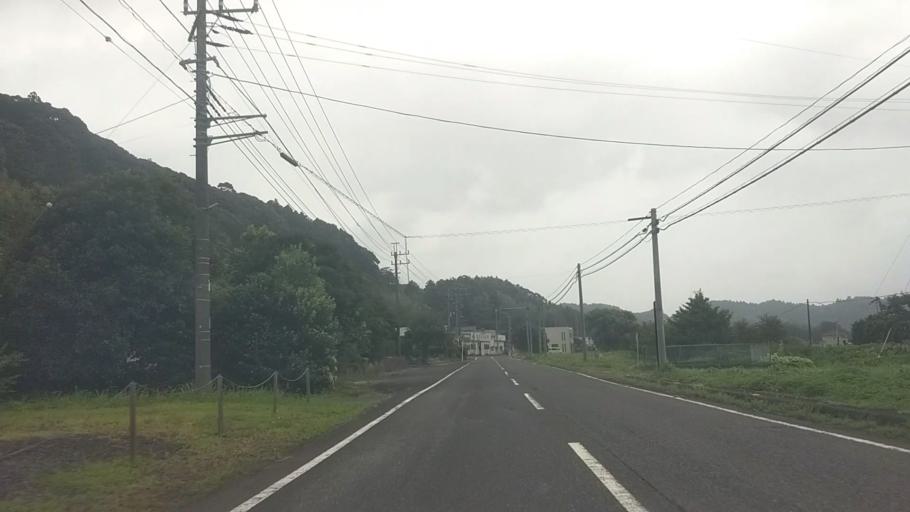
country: JP
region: Chiba
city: Ohara
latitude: 35.2610
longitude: 140.2499
